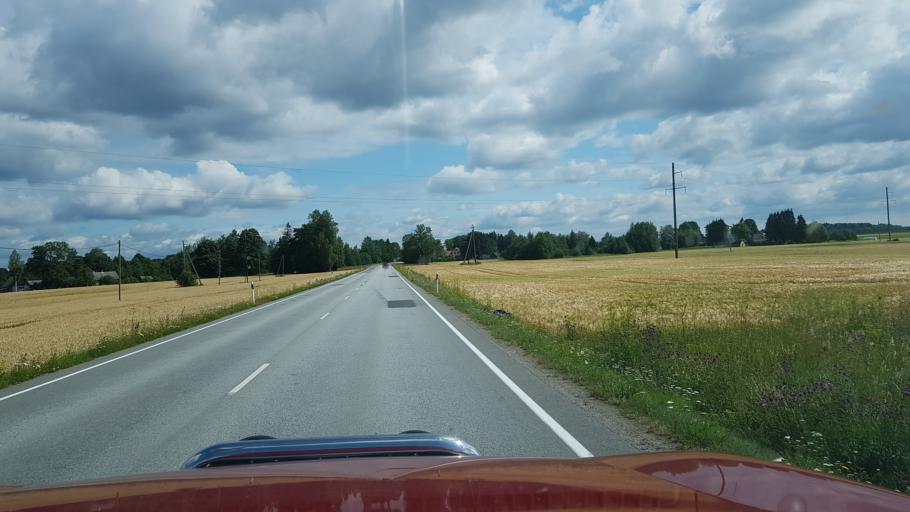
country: EE
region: Jogevamaa
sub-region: Jogeva linn
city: Jogeva
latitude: 58.8222
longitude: 26.5823
